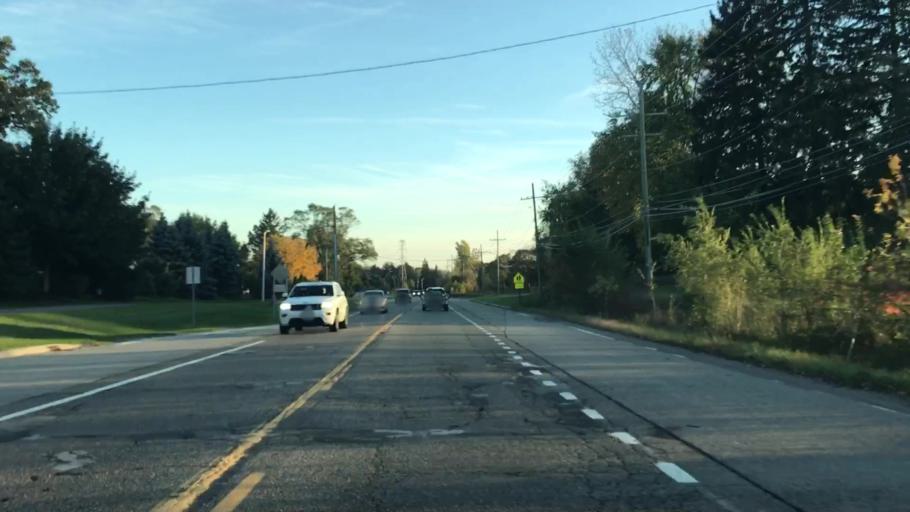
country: US
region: Michigan
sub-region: Oakland County
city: Rochester
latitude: 42.6795
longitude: -83.0940
